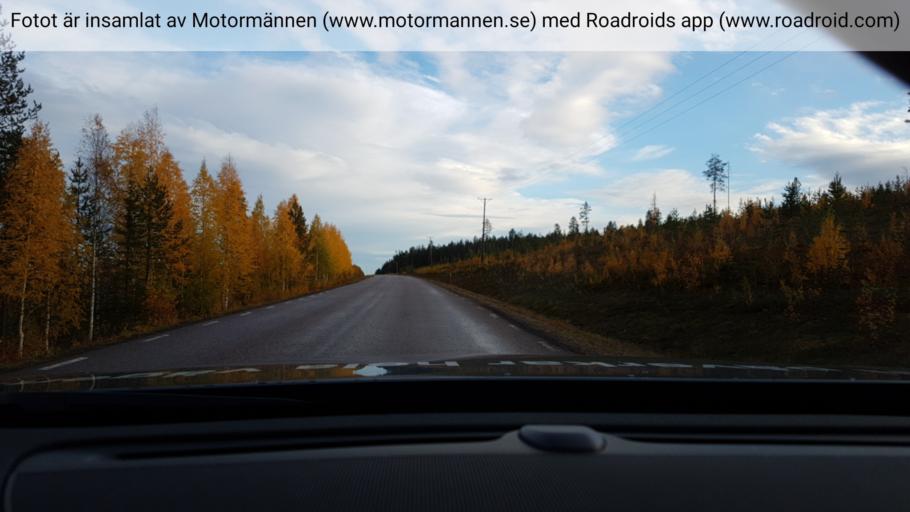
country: SE
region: Norrbotten
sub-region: Overkalix Kommun
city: OEverkalix
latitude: 67.0334
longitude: 22.5049
